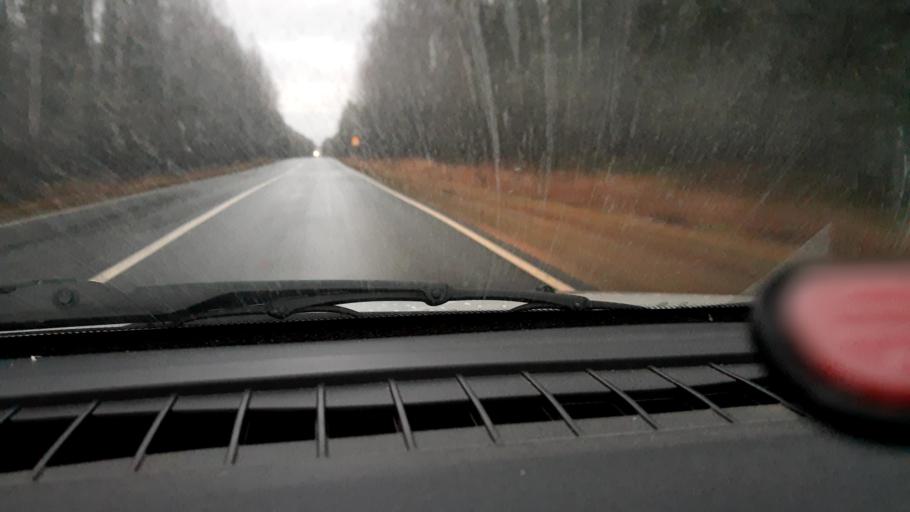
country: RU
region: Nizjnij Novgorod
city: Uren'
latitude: 57.2624
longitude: 45.6172
